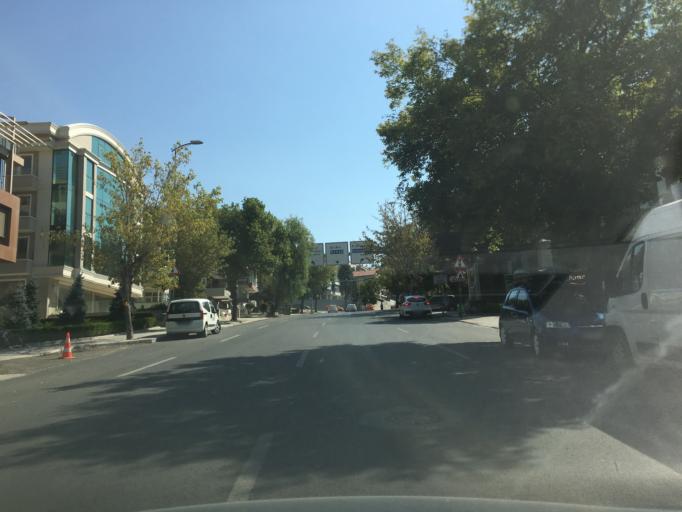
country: TR
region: Ankara
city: Cankaya
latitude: 39.8945
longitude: 32.8686
